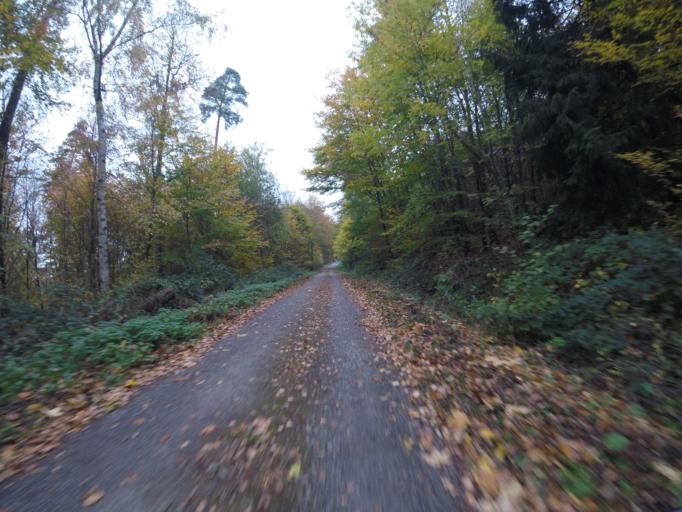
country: DE
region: Baden-Wuerttemberg
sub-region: Regierungsbezirk Stuttgart
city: Oberstenfeld
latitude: 48.9999
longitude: 9.3232
